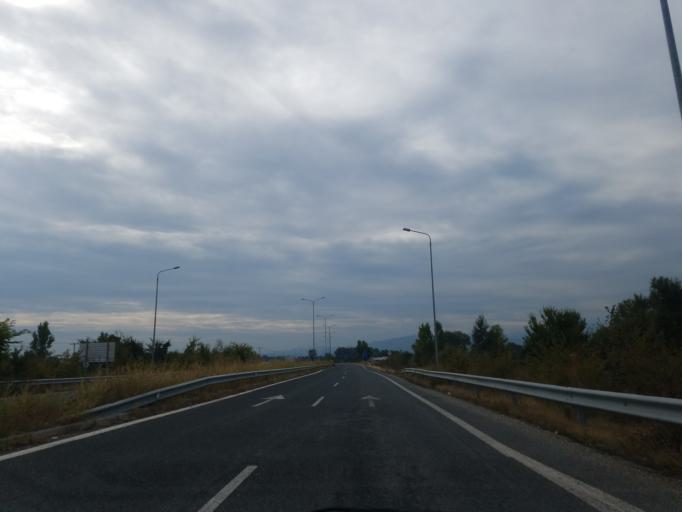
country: GR
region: Thessaly
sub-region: Trikala
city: Pyrgetos
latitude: 39.5403
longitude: 21.7357
